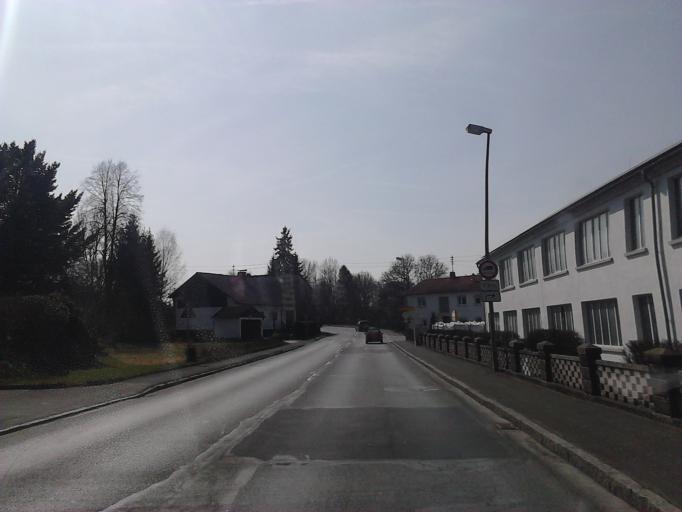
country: DE
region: Bavaria
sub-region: Upper Franconia
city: Marktrodach
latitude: 50.2701
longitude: 11.4089
